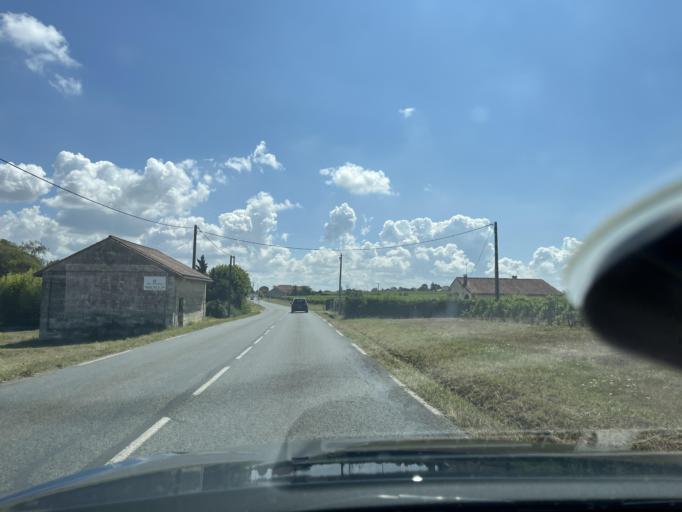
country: FR
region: Aquitaine
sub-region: Departement de la Gironde
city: Bourg
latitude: 45.0534
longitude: -0.5955
